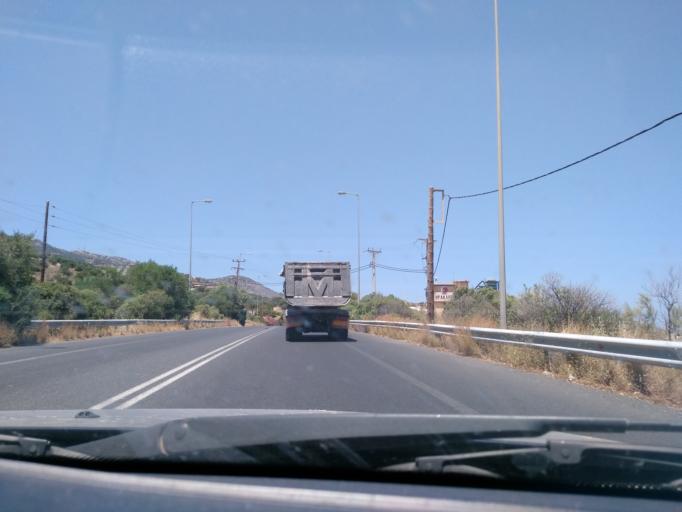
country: GR
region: Crete
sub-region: Nomos Irakleiou
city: Gazi
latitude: 35.3463
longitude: 25.0448
